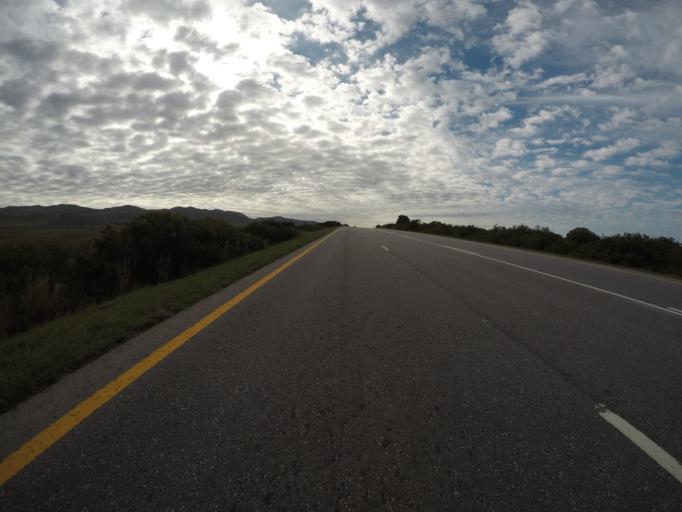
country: ZA
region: Eastern Cape
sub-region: Cacadu District Municipality
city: Kruisfontein
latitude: -34.0110
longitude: 24.6490
